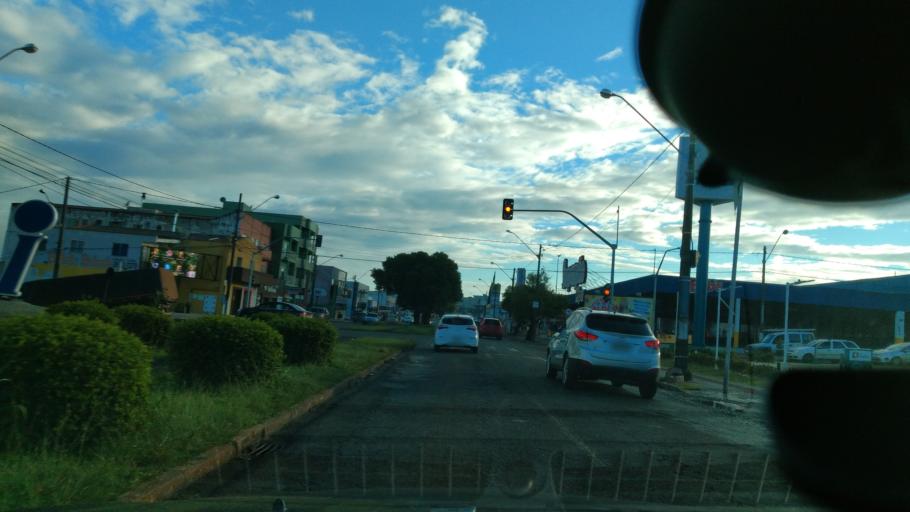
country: BR
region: Parana
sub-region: Guarapuava
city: Guarapuava
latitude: -25.3883
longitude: -51.4753
